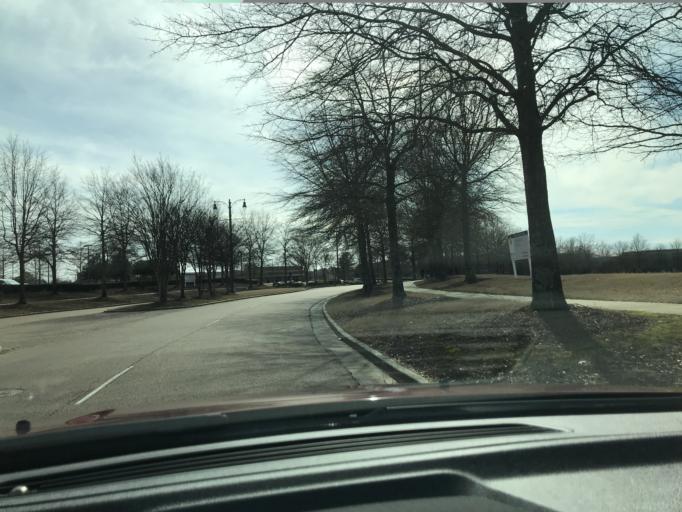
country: US
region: Tennessee
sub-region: Shelby County
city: Collierville
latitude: 35.0439
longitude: -89.7007
